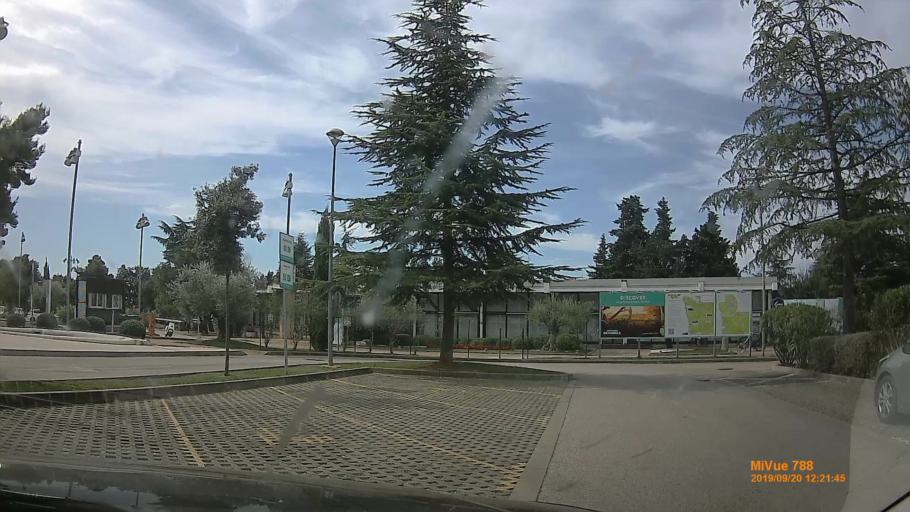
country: HR
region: Istarska
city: Novigrad
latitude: 45.3674
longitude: 13.5472
